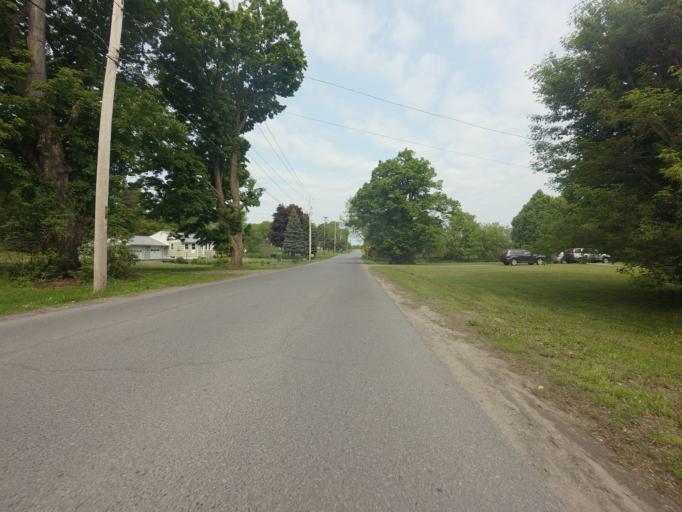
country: US
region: New York
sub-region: Jefferson County
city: Watertown
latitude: 43.9742
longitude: -75.8740
